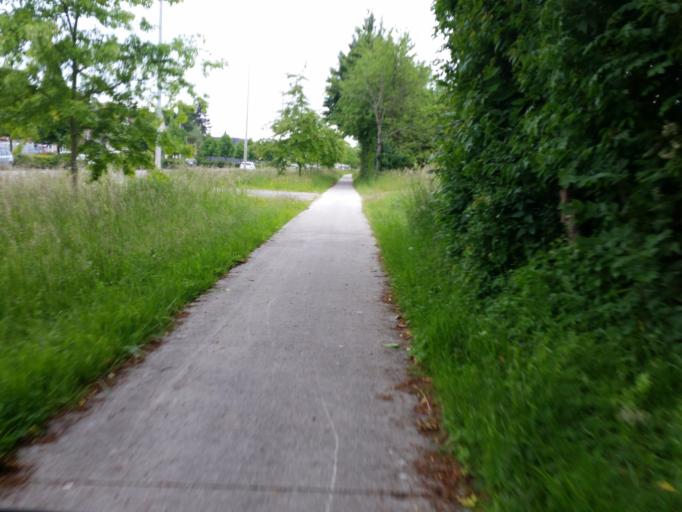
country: BE
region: Flanders
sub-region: Provincie Vlaams-Brabant
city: Zemst
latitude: 50.9572
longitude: 4.4549
